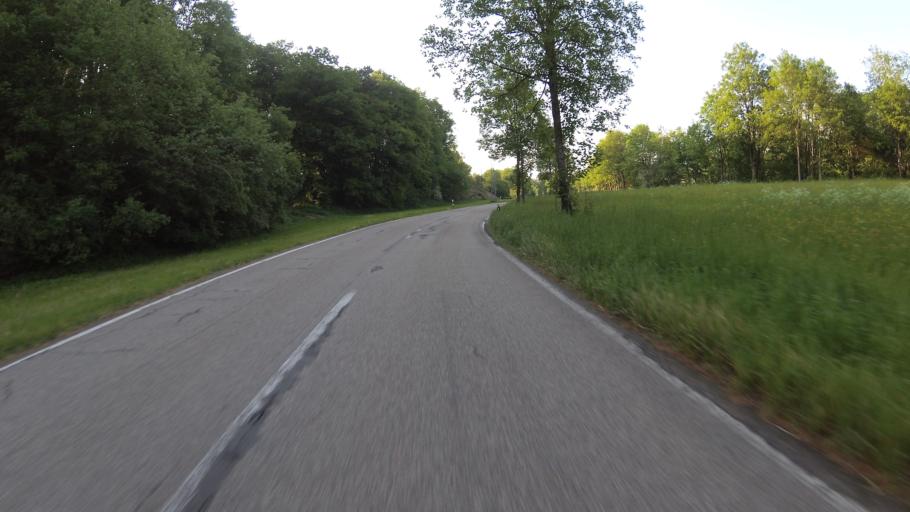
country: DE
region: Rheinland-Pfalz
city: Contwig
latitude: 49.2200
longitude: 7.4182
